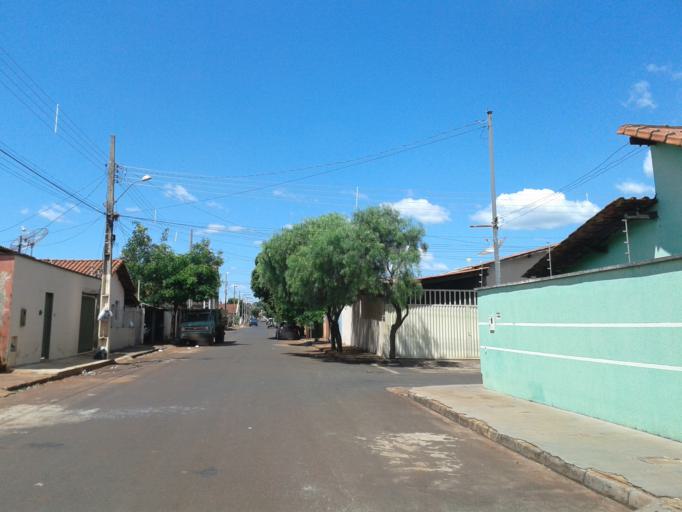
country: BR
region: Minas Gerais
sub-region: Centralina
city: Centralina
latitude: -18.7266
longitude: -49.1959
